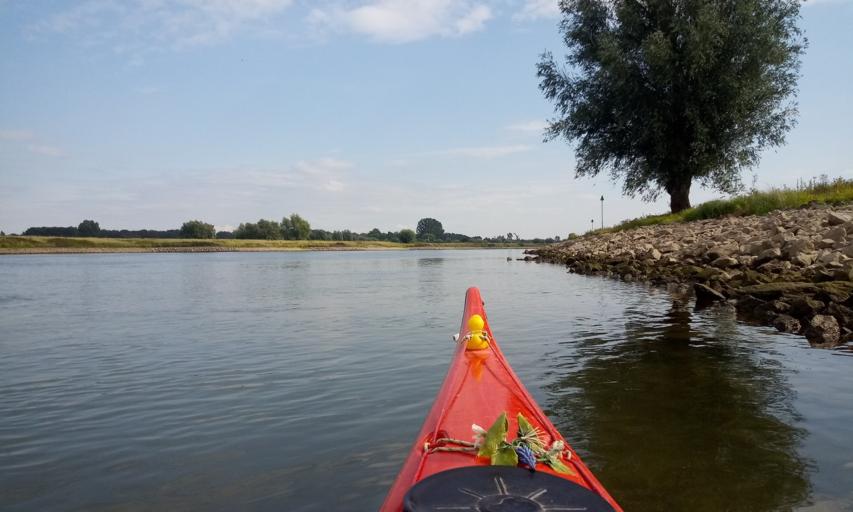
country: NL
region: Gelderland
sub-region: Gemeente Lochem
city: Gorssel
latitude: 52.1784
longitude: 6.1906
